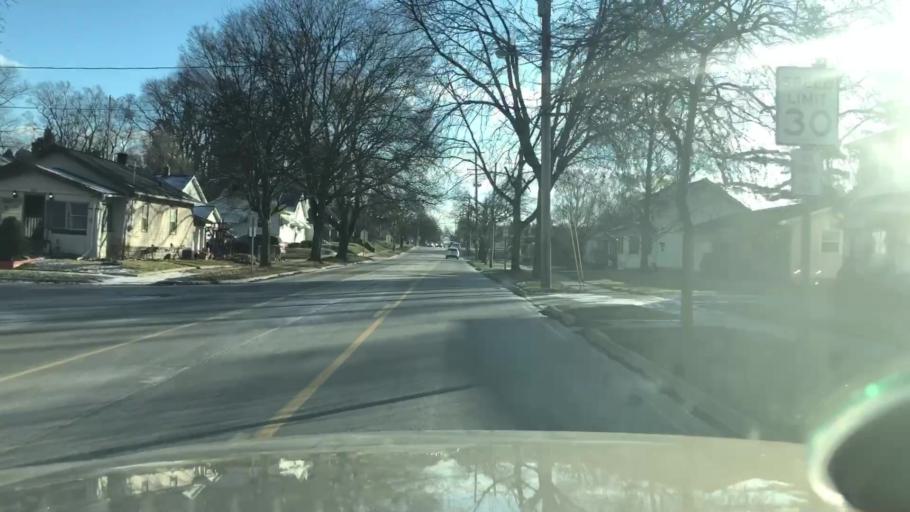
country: US
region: Michigan
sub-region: Jackson County
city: Jackson
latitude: 42.2357
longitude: -84.4233
